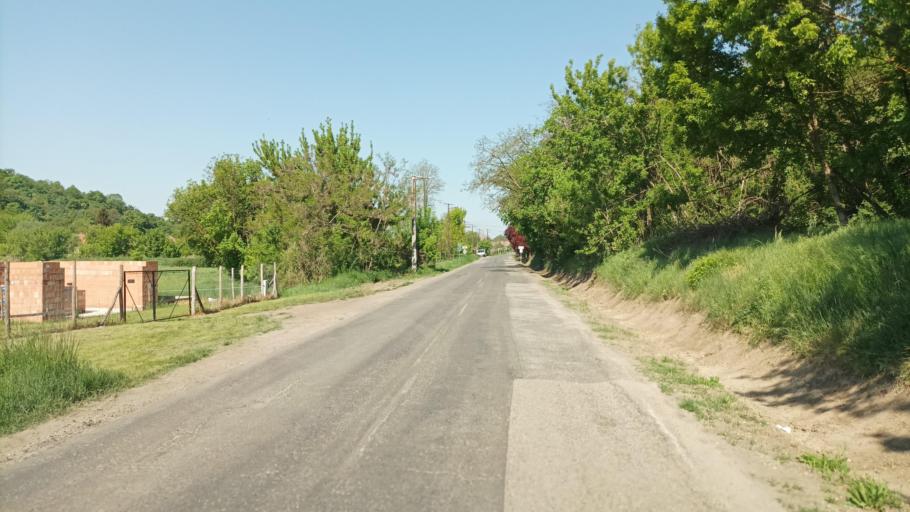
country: HU
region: Pest
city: Gomba
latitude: 47.3529
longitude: 19.5538
